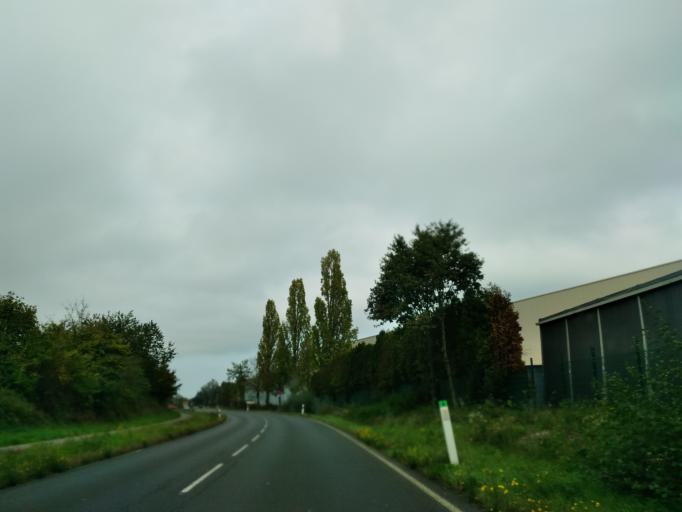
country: DE
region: North Rhine-Westphalia
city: Sankt Augustin
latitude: 50.7503
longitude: 7.1599
